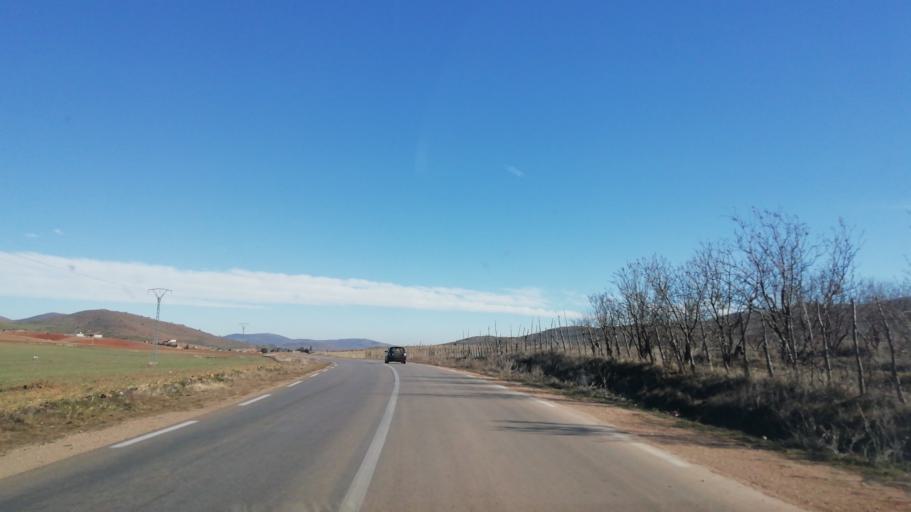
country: DZ
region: Tlemcen
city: Sebdou
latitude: 34.7337
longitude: -1.1769
